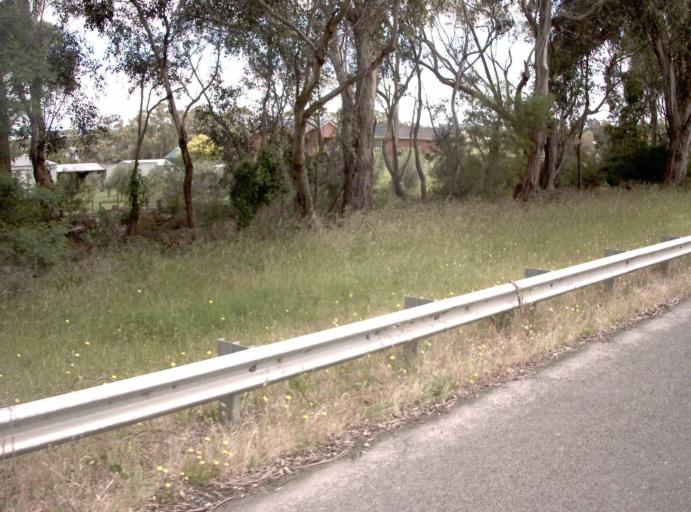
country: AU
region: Victoria
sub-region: Cardinia
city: Koo-Wee-Rup
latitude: -38.3852
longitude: 145.5491
